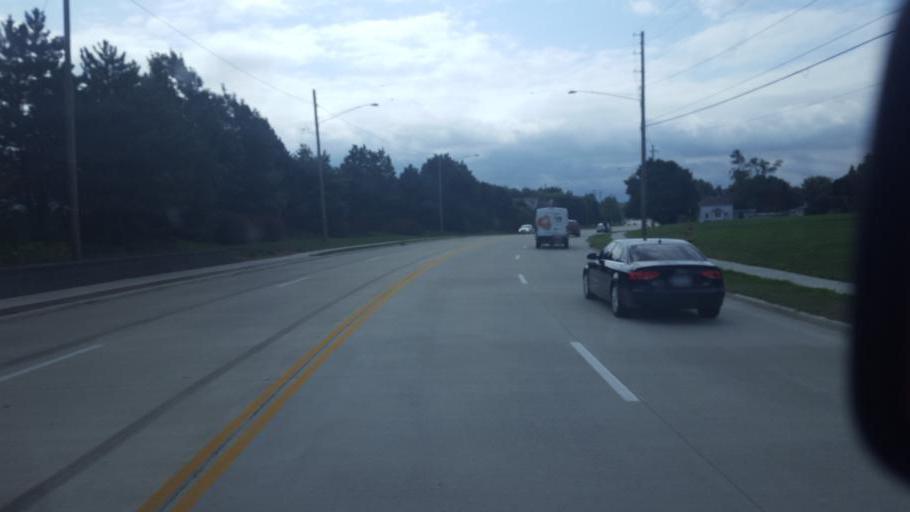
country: US
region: Ohio
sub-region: Lake County
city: Mentor
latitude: 41.6864
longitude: -81.3039
